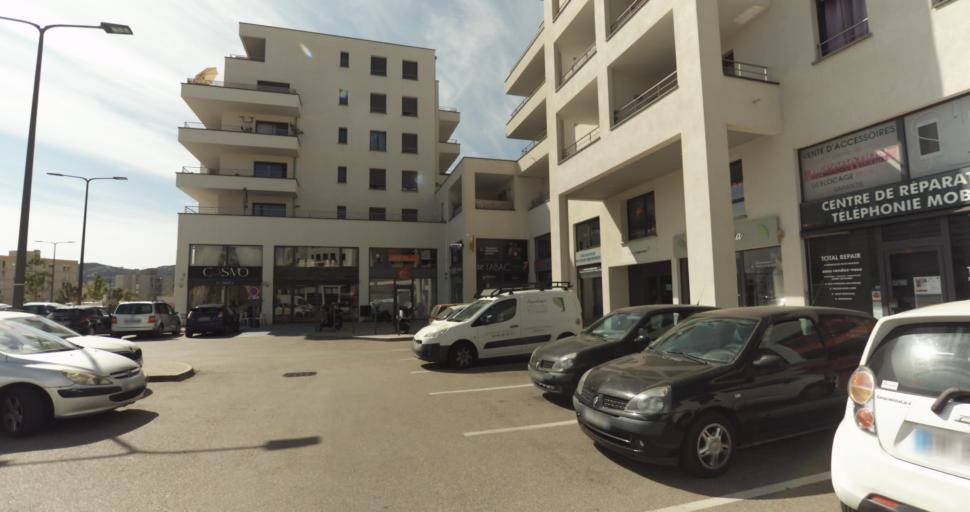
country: FR
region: Corsica
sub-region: Departement de la Corse-du-Sud
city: Ajaccio
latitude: 41.9426
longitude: 8.7498
